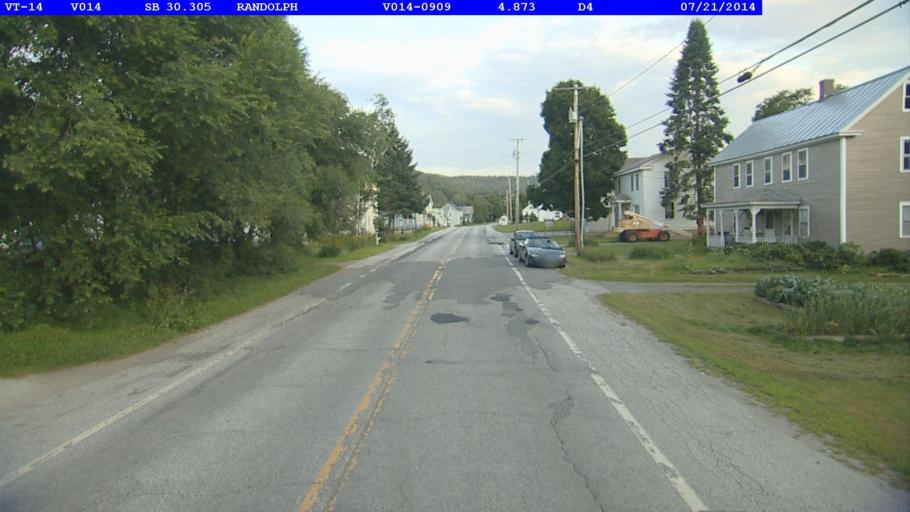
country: US
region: Vermont
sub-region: Orange County
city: Randolph
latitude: 43.9395
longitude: -72.5538
